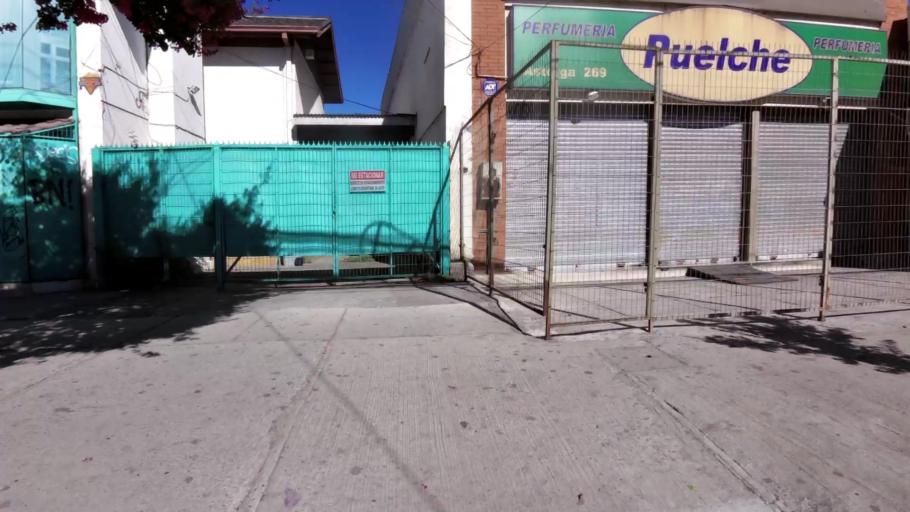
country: CL
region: O'Higgins
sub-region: Provincia de Cachapoal
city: Rancagua
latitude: -34.1685
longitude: -70.7432
